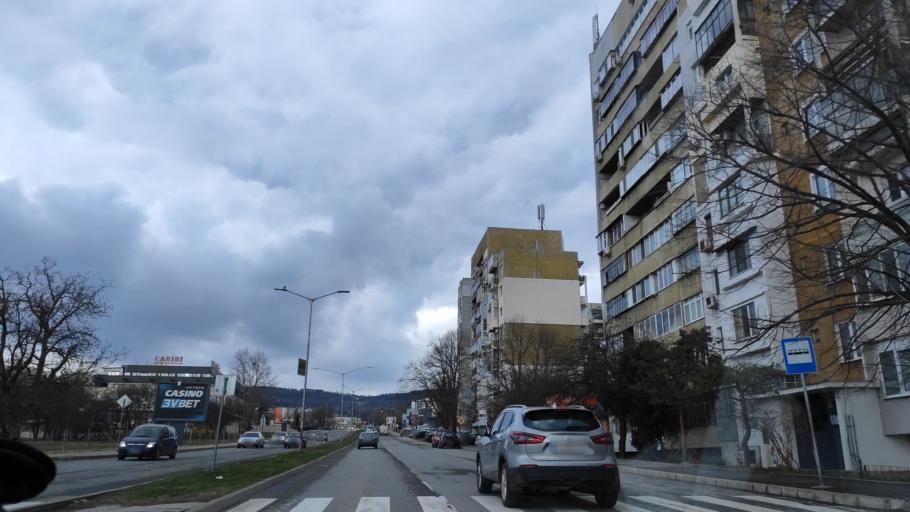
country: BG
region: Varna
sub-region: Obshtina Varna
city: Varna
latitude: 43.2319
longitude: 27.8798
